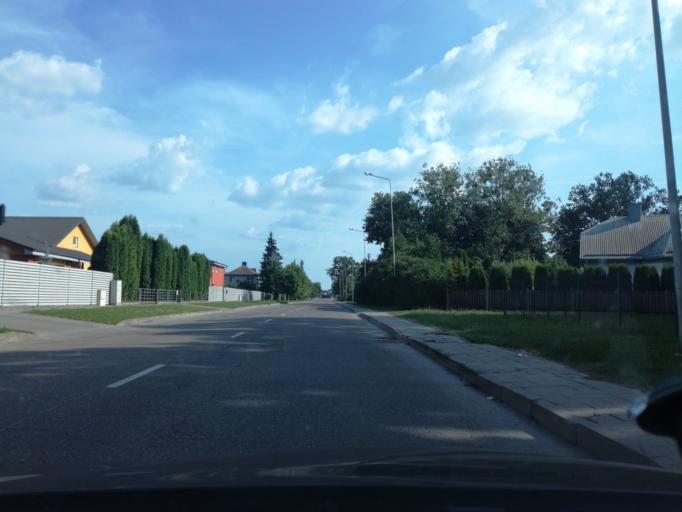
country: LT
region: Marijampoles apskritis
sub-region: Marijampole Municipality
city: Marijampole
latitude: 54.5442
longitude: 23.3484
